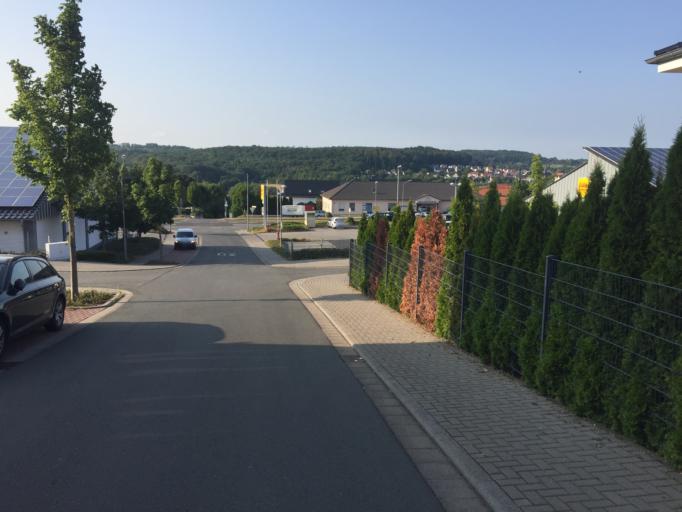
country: DE
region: Hesse
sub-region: Regierungsbezirk Giessen
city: Langgons
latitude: 50.5374
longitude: 8.7289
